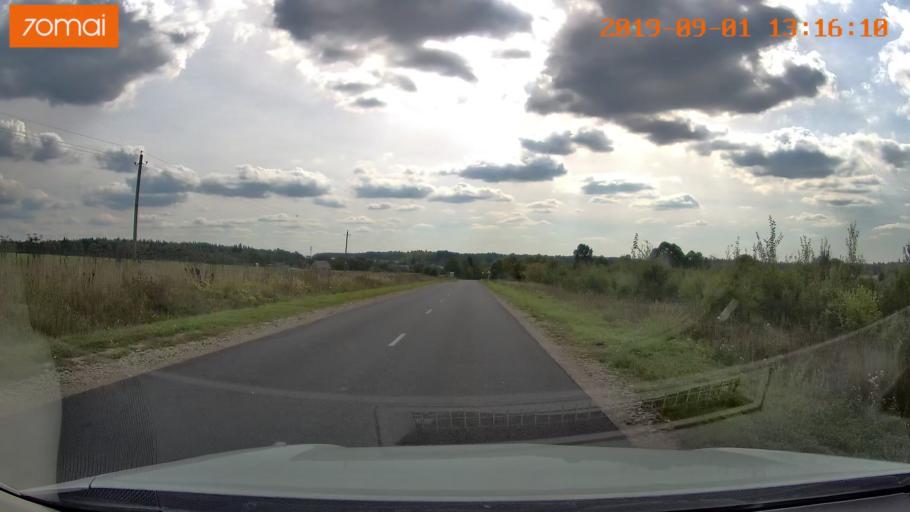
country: RU
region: Kaluga
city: Maloyaroslavets
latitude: 54.9477
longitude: 36.4586
